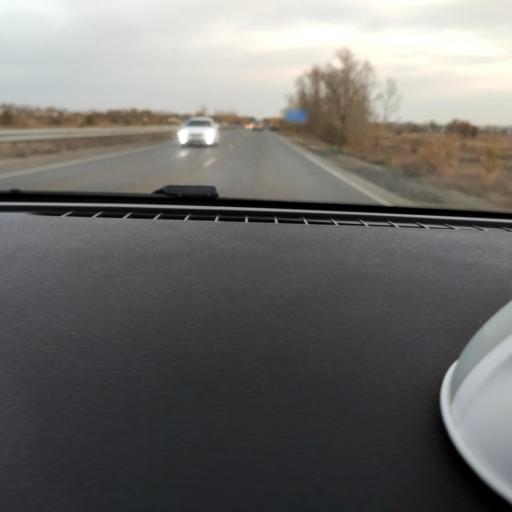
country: RU
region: Samara
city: Samara
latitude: 53.0964
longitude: 50.1462
